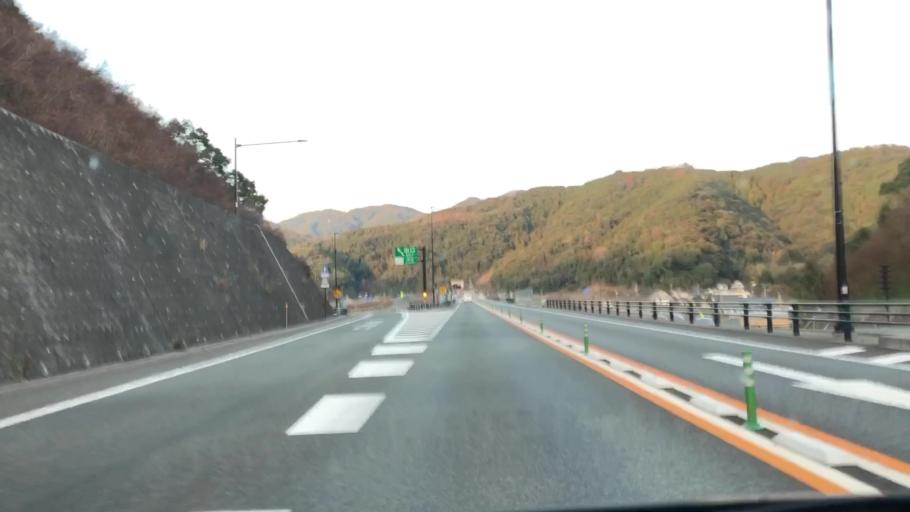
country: JP
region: Kumamoto
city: Minamata
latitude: 32.2962
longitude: 130.5083
